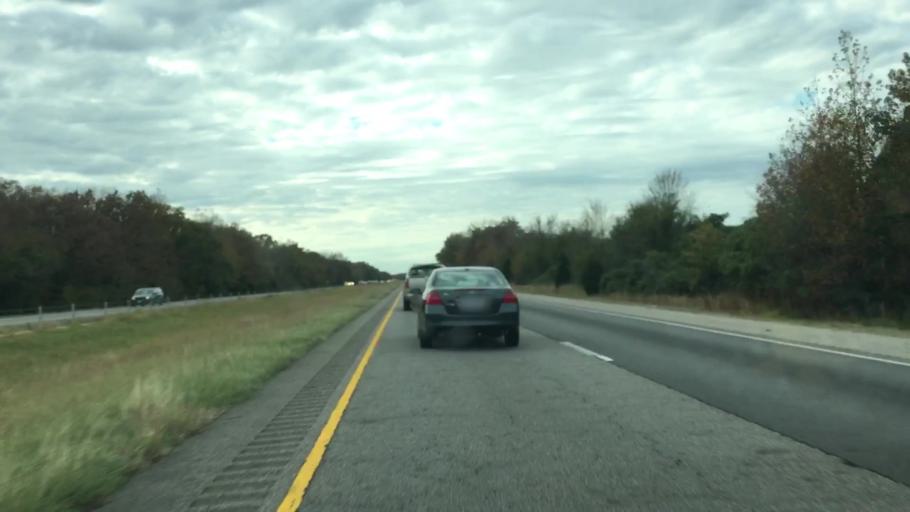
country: US
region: Arkansas
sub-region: Conway County
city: Morrilton
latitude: 35.1604
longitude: -92.5932
